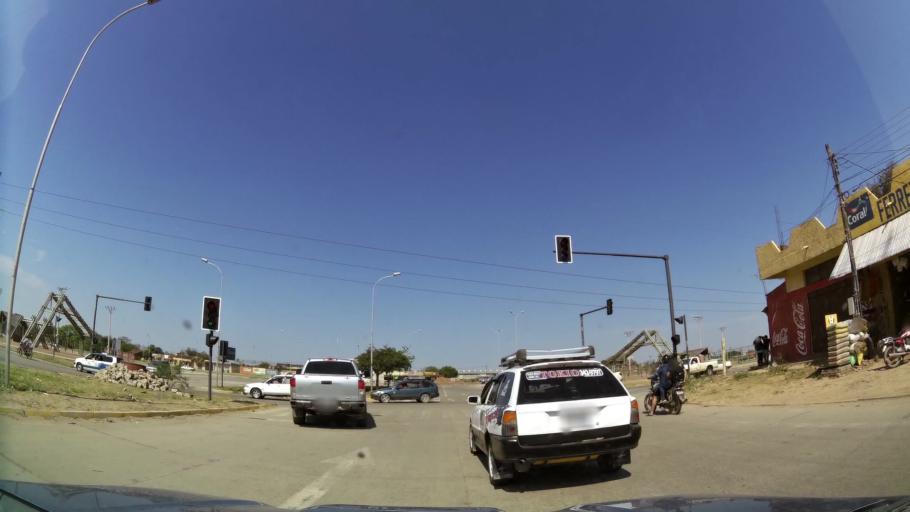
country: BO
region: Santa Cruz
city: Santa Cruz de la Sierra
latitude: -17.7362
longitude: -63.1427
